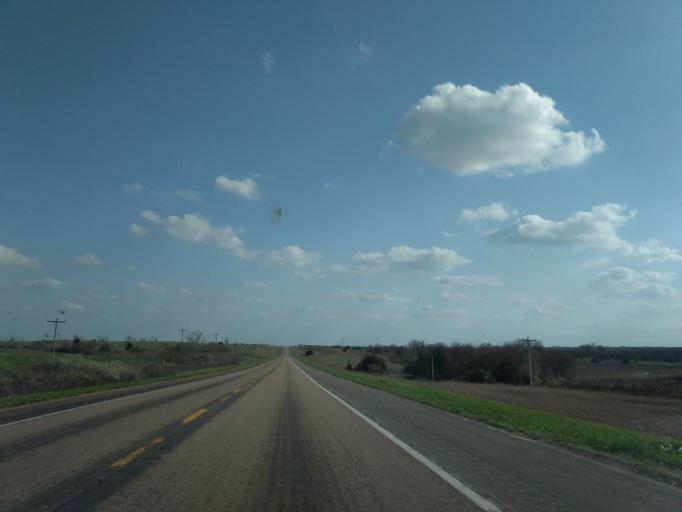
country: US
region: Nebraska
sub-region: Webster County
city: Red Cloud
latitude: 40.1376
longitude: -98.5190
